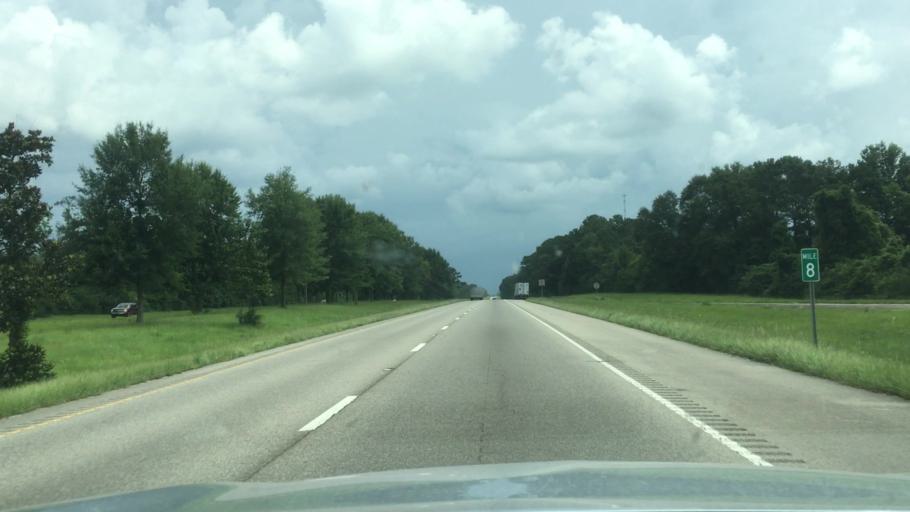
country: US
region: Mississippi
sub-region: Pearl River County
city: Carriere
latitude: 30.5652
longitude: -89.6374
